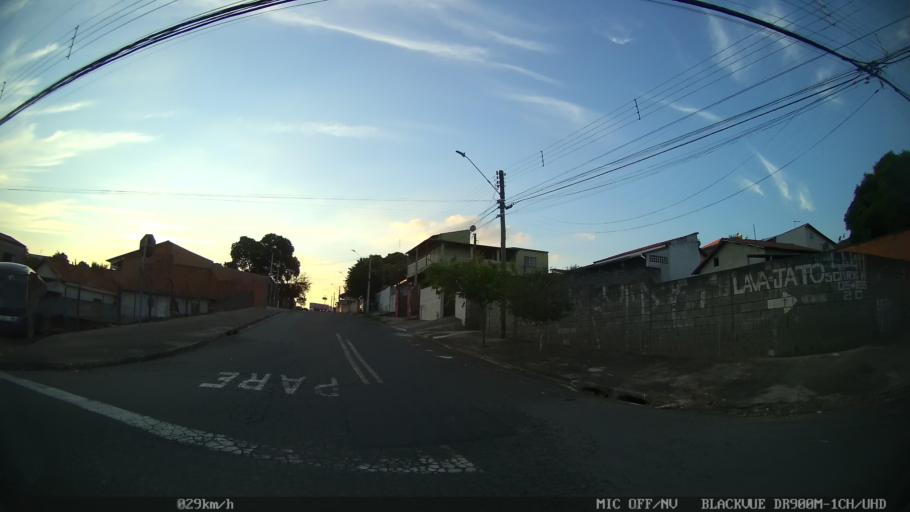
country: BR
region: Sao Paulo
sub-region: Hortolandia
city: Hortolandia
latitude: -22.8515
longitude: -47.2148
